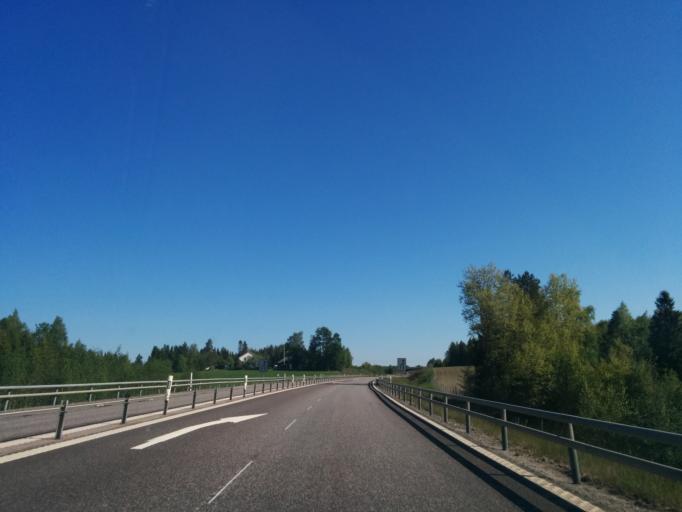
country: SE
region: Vaesternorrland
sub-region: Haernoesands Kommun
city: Haernoesand
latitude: 62.7548
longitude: 17.9022
